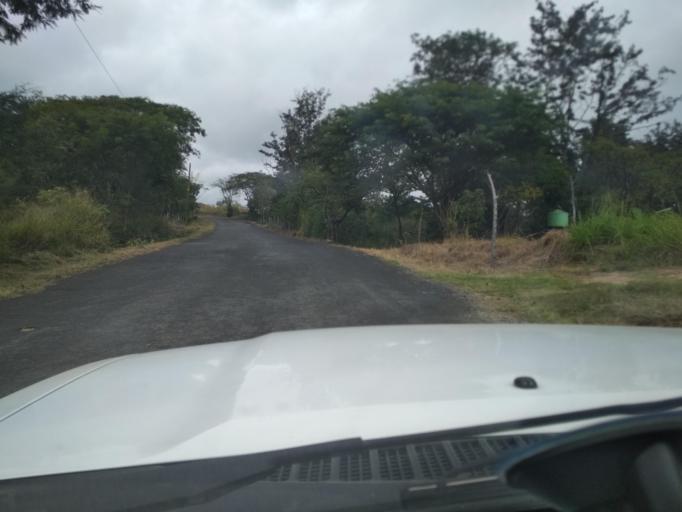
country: MX
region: Veracruz
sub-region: Emiliano Zapata
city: Dos Rios
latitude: 19.5331
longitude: -96.8077
